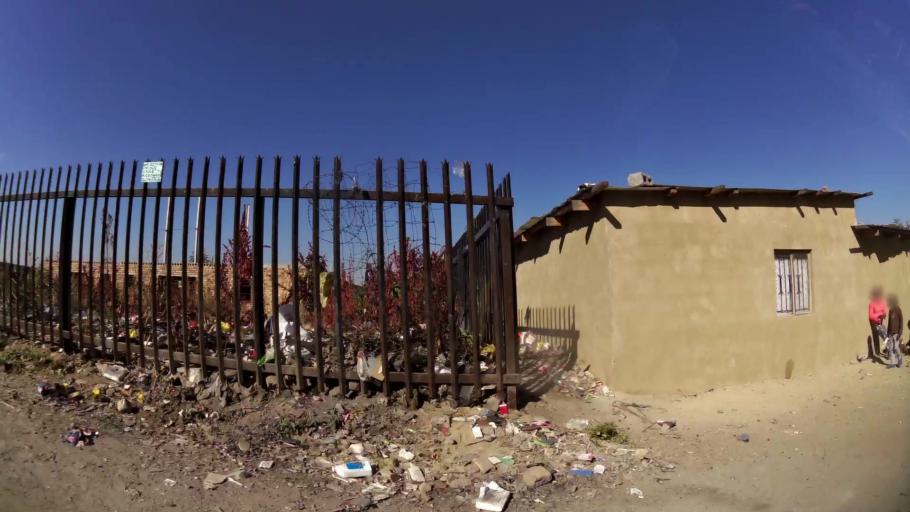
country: ZA
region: Gauteng
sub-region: City of Johannesburg Metropolitan Municipality
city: Modderfontein
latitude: -26.1073
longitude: 28.1212
